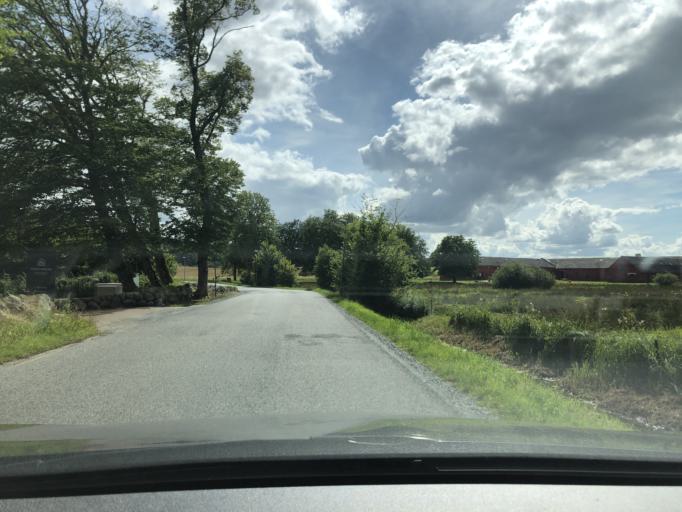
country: DK
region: South Denmark
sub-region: Vejle Kommune
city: Jelling
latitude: 55.7033
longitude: 9.4376
